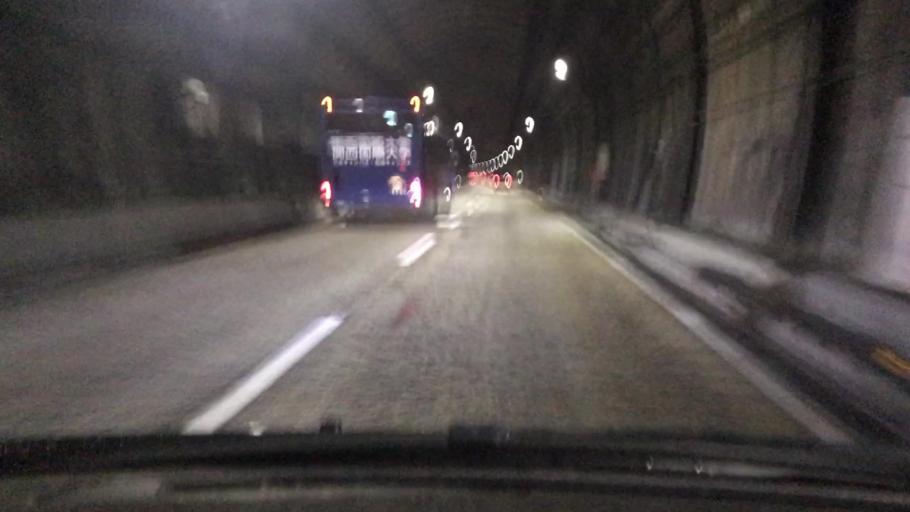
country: JP
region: Hyogo
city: Kobe
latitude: 34.7162
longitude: 135.1888
